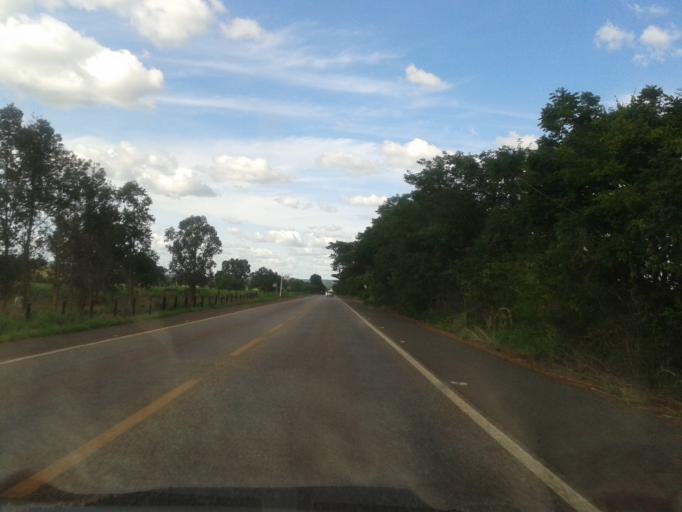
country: BR
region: Goias
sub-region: Mozarlandia
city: Mozarlandia
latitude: -15.0263
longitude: -50.5993
